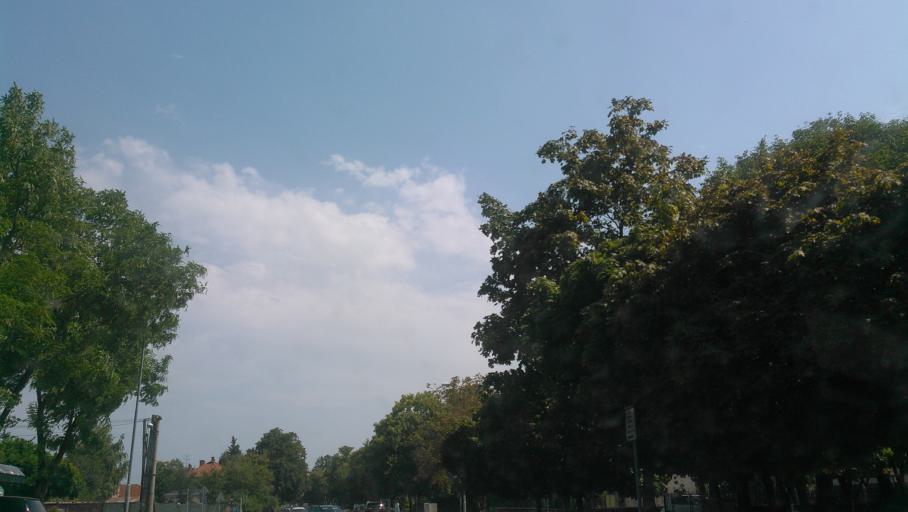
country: SK
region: Trnavsky
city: Dunajska Streda
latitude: 48.0005
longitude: 17.6062
